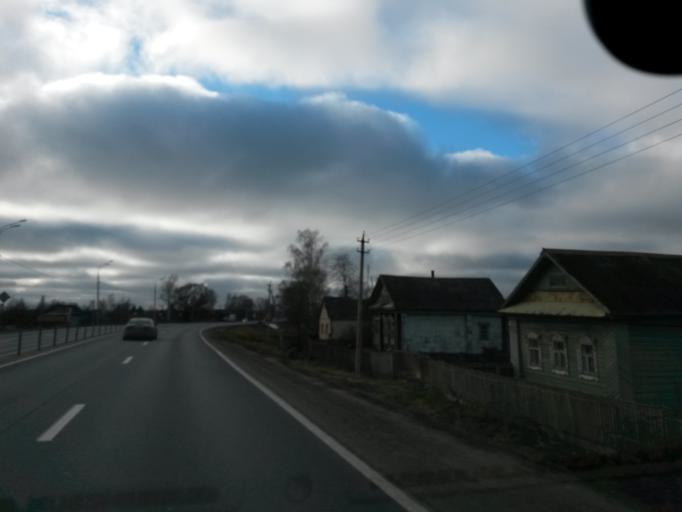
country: RU
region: Jaroslavl
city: Semibratovo
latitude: 57.3163
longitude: 39.5582
